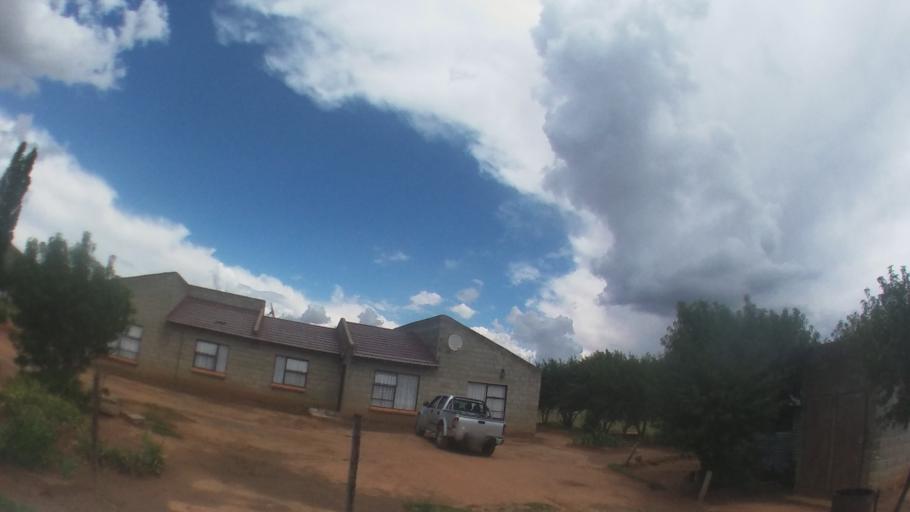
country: LS
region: Maseru
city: Nako
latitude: -29.6216
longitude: 27.5022
